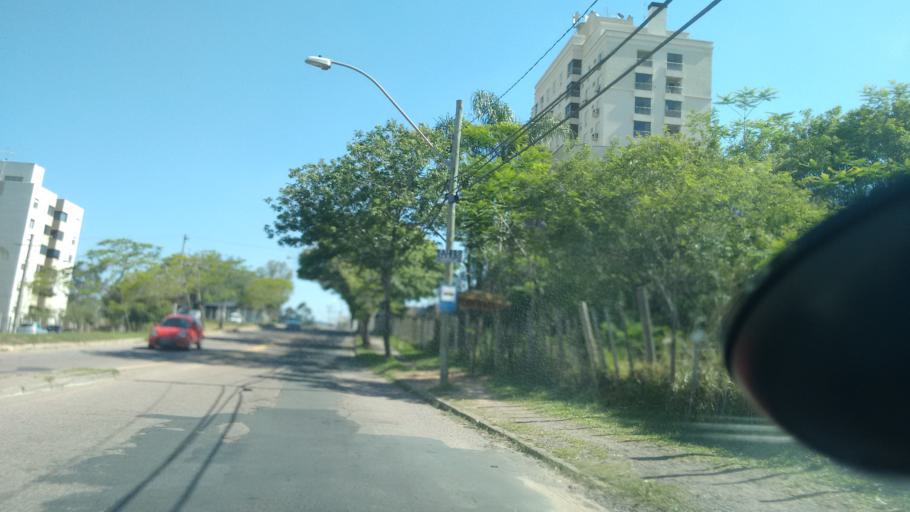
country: BR
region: Rio Grande do Sul
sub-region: Cachoeirinha
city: Cachoeirinha
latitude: -30.0036
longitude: -51.1276
